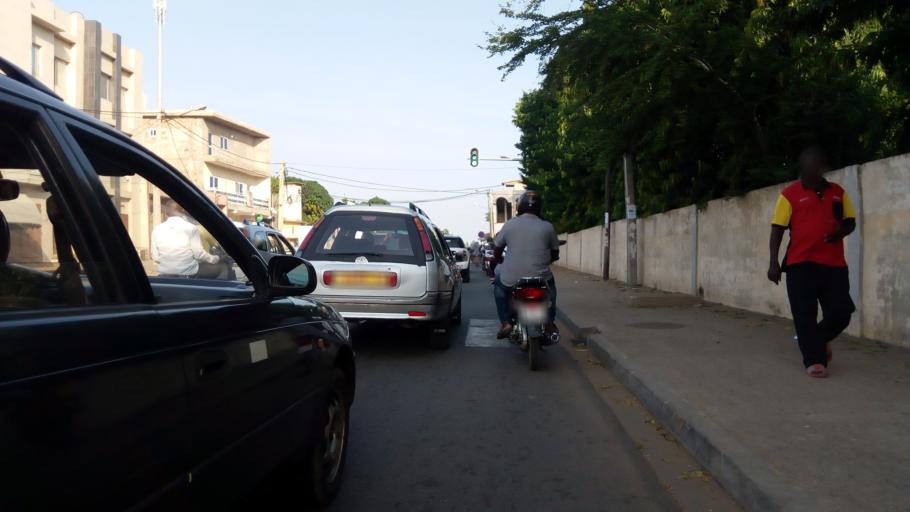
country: TG
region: Maritime
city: Lome
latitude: 6.1460
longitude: 1.2042
